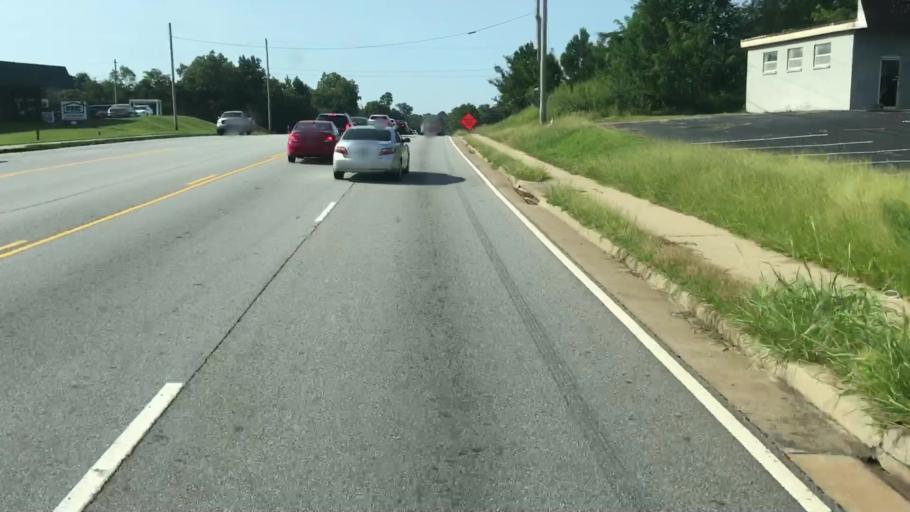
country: US
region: Georgia
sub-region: Gwinnett County
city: Lawrenceville
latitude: 33.9605
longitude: -83.9857
